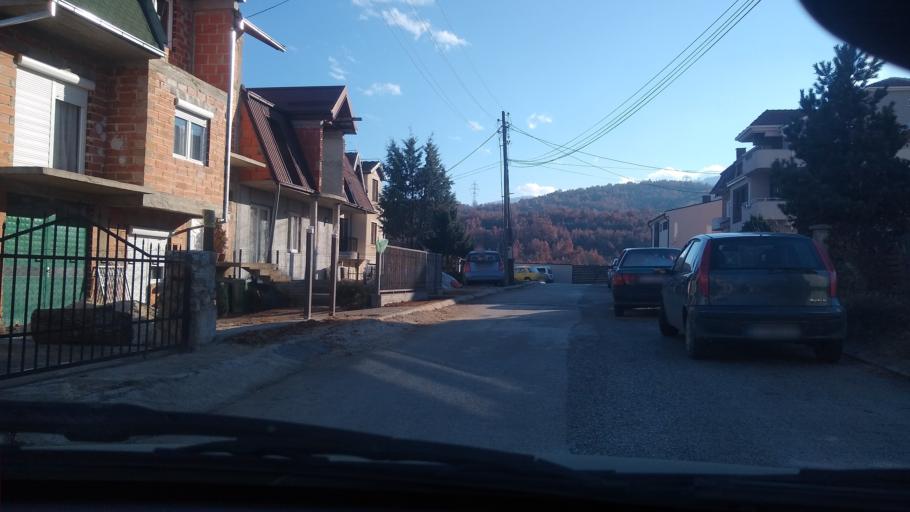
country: MK
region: Bitola
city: Bitola
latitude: 41.0176
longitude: 21.3145
